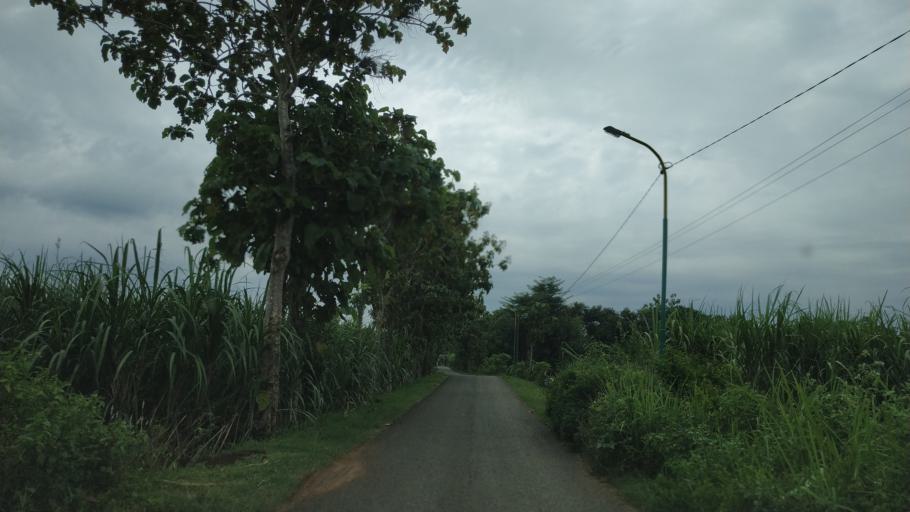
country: ID
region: Central Java
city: Krajan Tegalombo
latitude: -6.4250
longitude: 110.9844
